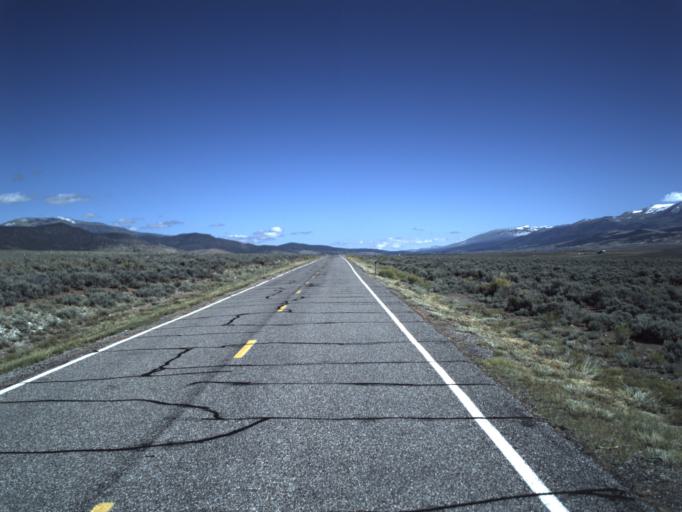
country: US
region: Utah
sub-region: Wayne County
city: Loa
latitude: 38.3734
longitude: -111.9382
